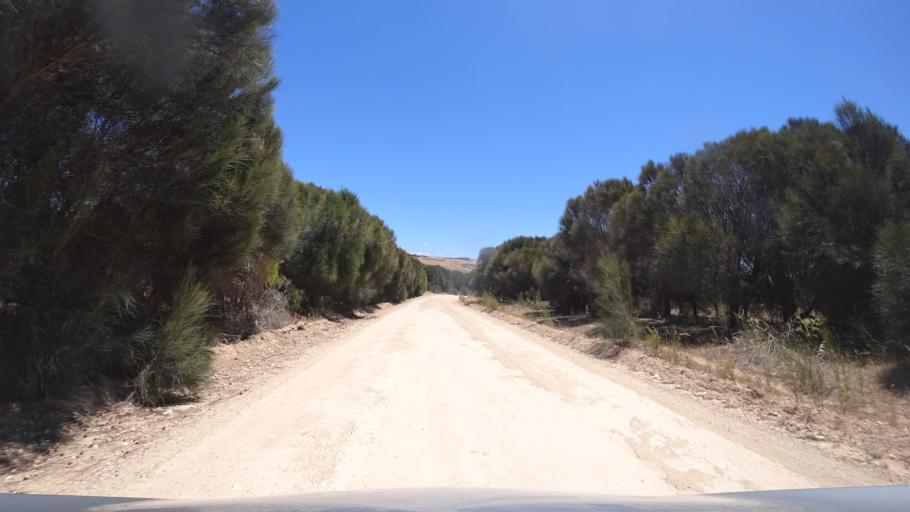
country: AU
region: South Australia
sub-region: Kangaroo Island
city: Kingscote
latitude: -35.6701
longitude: 137.0944
